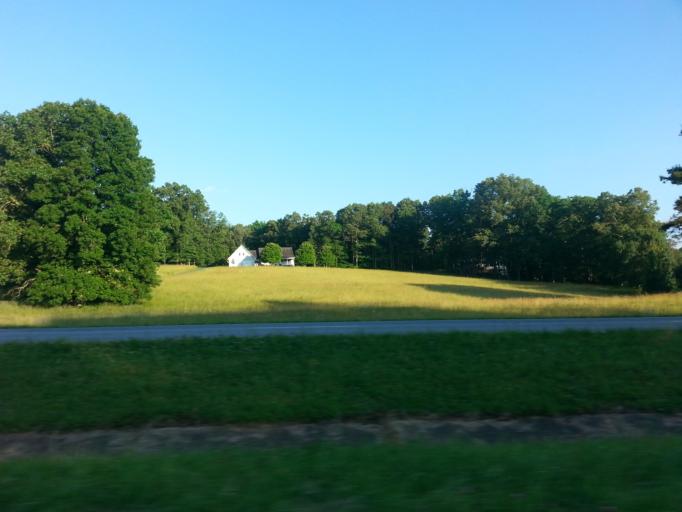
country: US
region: North Carolina
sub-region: Cherokee County
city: Murphy
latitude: 35.0298
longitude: -84.1069
